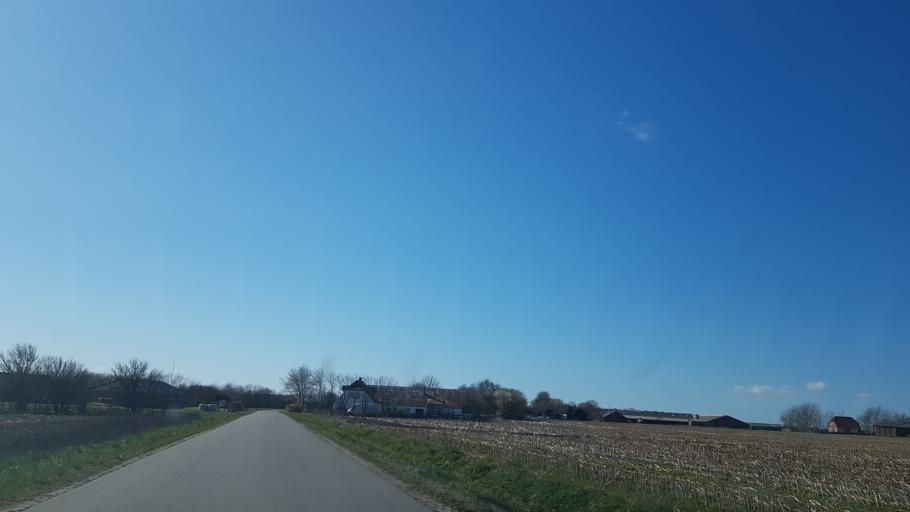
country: DK
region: South Denmark
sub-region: Esbjerg Kommune
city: Ribe
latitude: 55.2549
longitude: 8.6926
